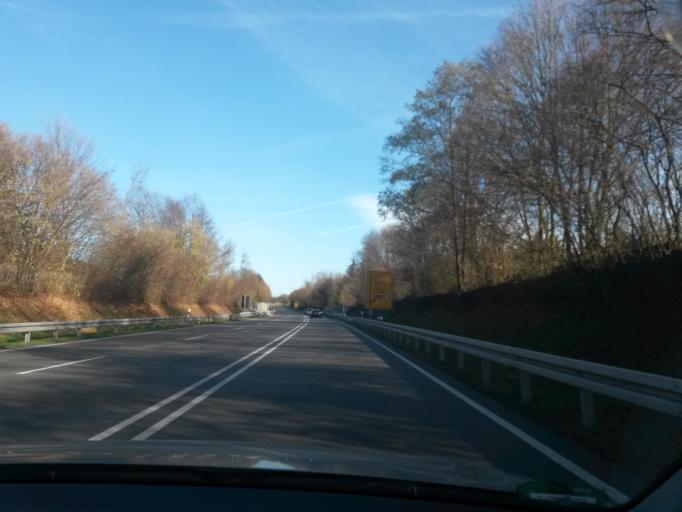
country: DE
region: Baden-Wuerttemberg
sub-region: Freiburg Region
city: Waldkirch
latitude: 48.0920
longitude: 7.9728
